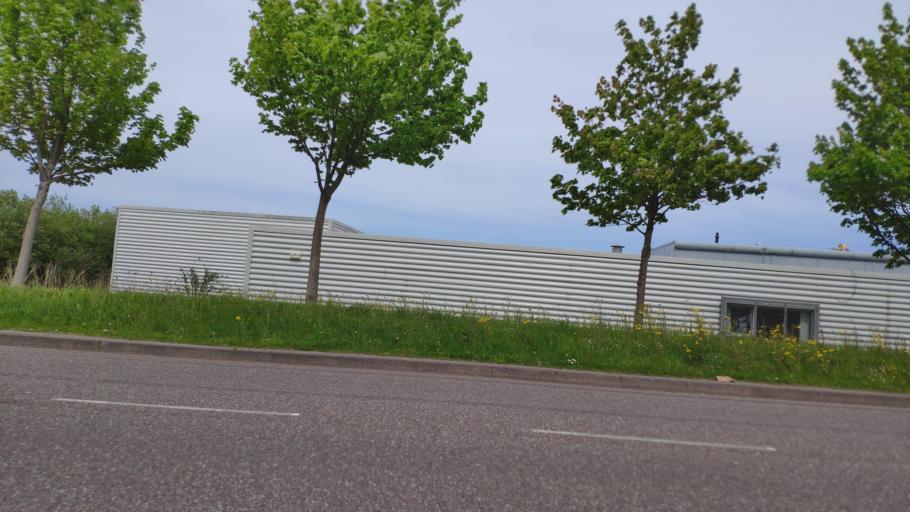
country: IE
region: Munster
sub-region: County Cork
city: Cork
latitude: 51.9146
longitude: -8.4640
